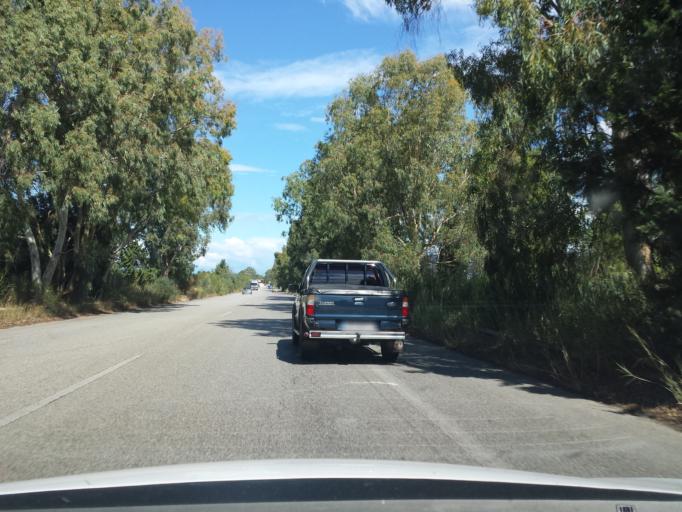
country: GR
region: West Greece
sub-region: Nomos Achaias
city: Kato Achaia
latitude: 38.1263
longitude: 21.5413
